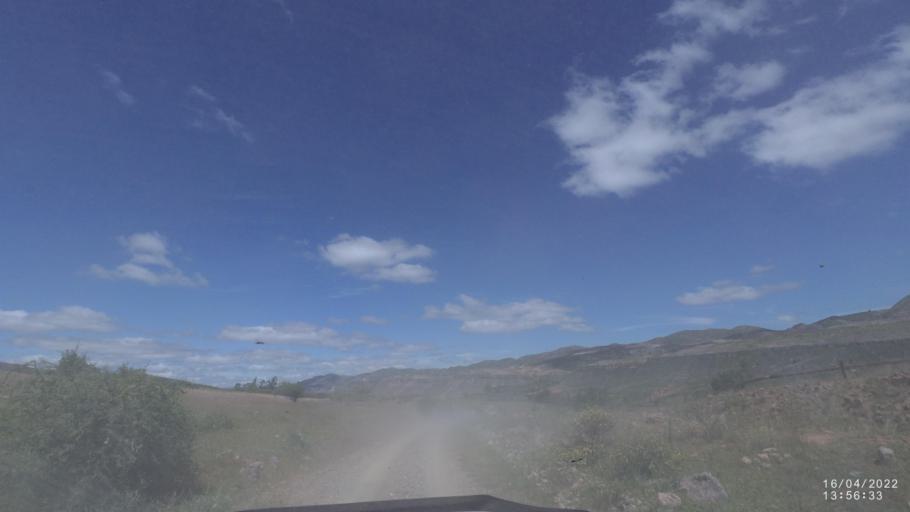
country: BO
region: Cochabamba
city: Mizque
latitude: -18.0322
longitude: -65.5646
